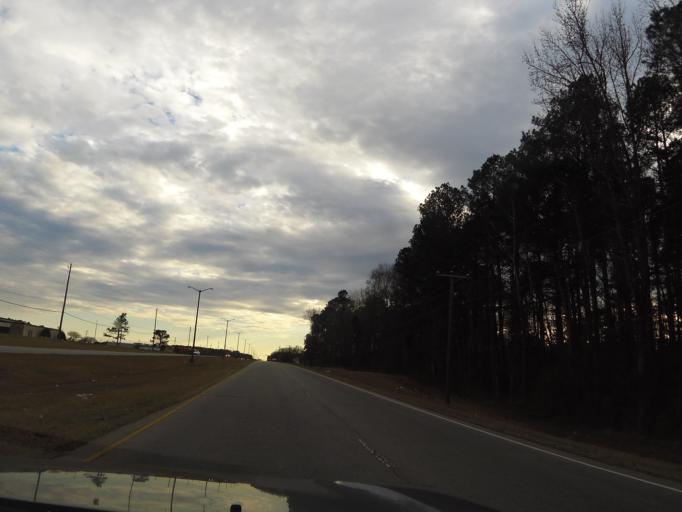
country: US
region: North Carolina
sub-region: Nash County
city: Rocky Mount
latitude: 36.0266
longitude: -77.7681
